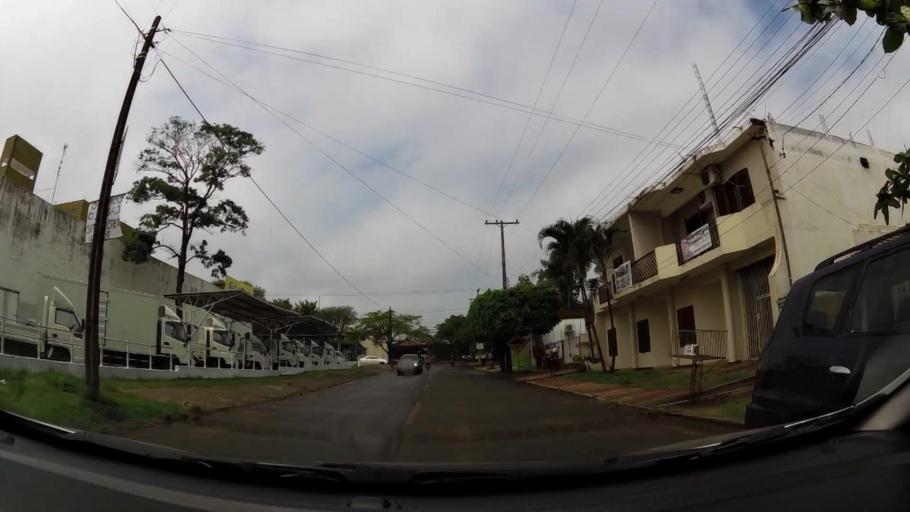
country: PY
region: Alto Parana
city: Presidente Franco
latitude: -25.5145
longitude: -54.6453
